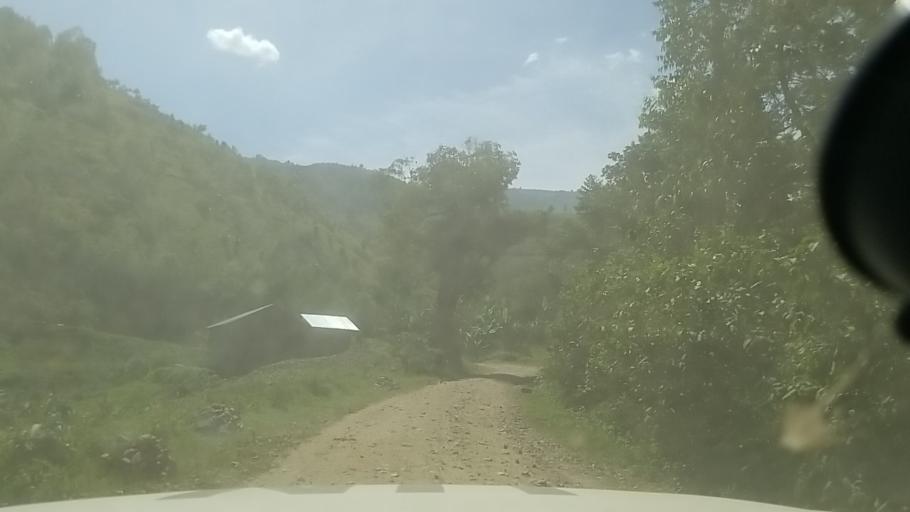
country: CD
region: Nord Kivu
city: Sake
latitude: -1.9548
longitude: 28.9216
